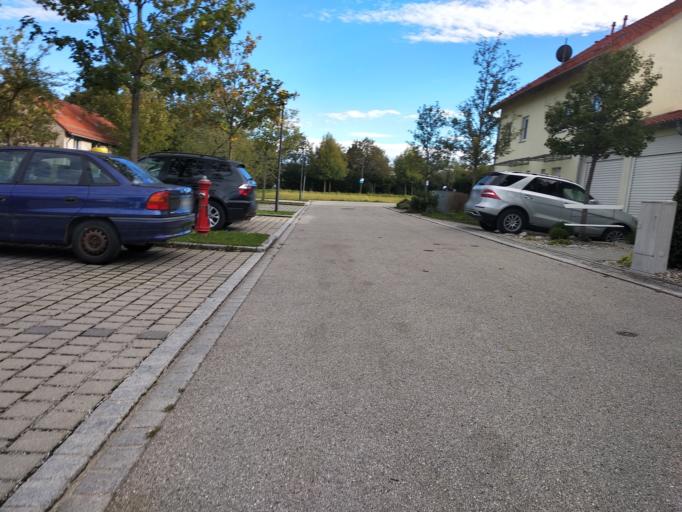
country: DE
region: Bavaria
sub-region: Upper Bavaria
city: Feldkirchen
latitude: 48.1455
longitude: 11.7242
